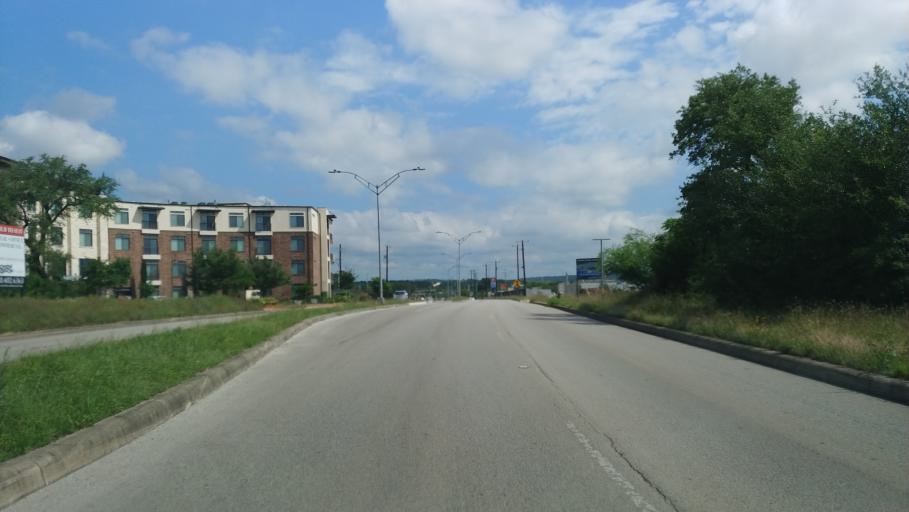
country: US
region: Texas
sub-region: Bexar County
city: Shavano Park
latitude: 29.5881
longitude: -98.5890
